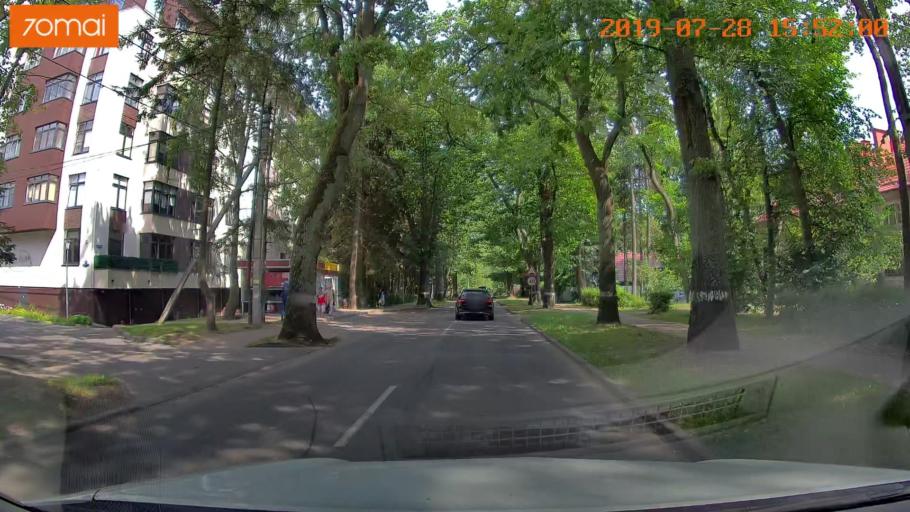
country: RU
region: Kaliningrad
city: Otradnoye
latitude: 54.9409
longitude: 20.1098
